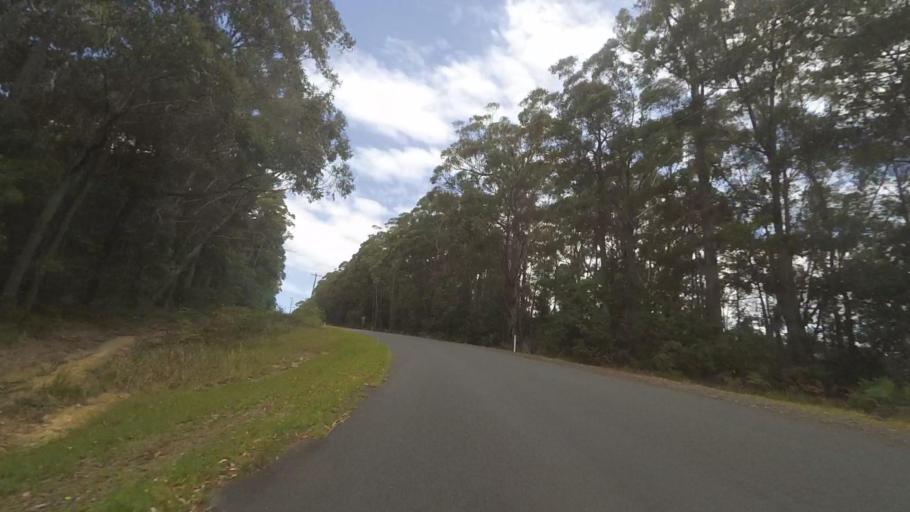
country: AU
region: New South Wales
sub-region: Shoalhaven Shire
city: Milton
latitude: -35.3844
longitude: 150.3654
